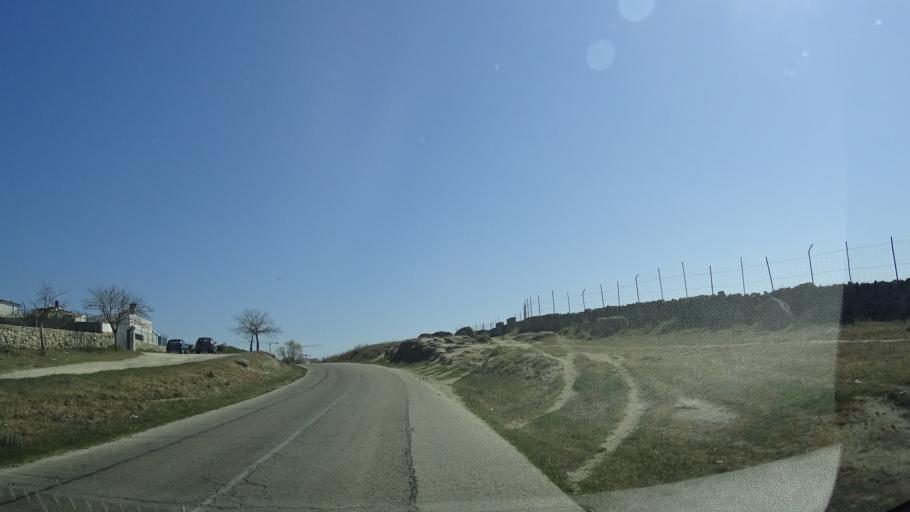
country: ES
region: Madrid
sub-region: Provincia de Madrid
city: Colmenar Viejo
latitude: 40.6483
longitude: -3.7995
